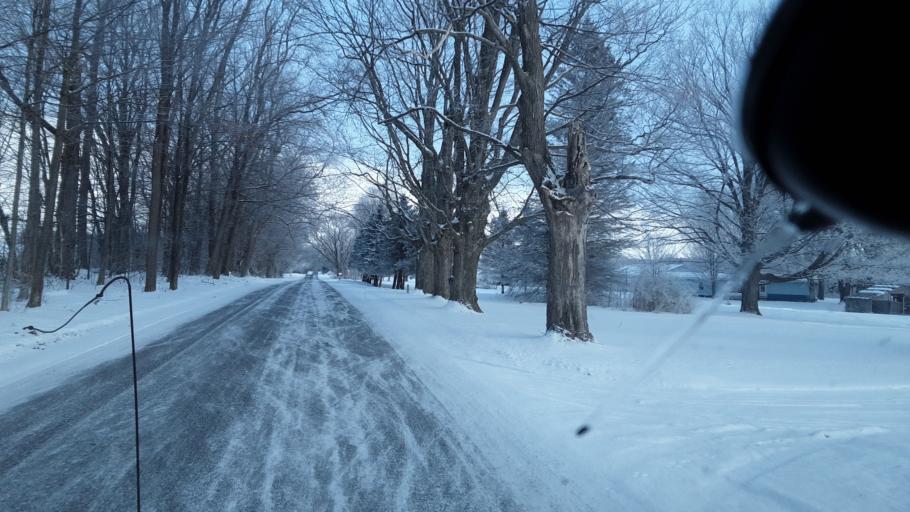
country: US
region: Michigan
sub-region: Ingham County
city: Leslie
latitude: 42.4404
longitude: -84.4970
